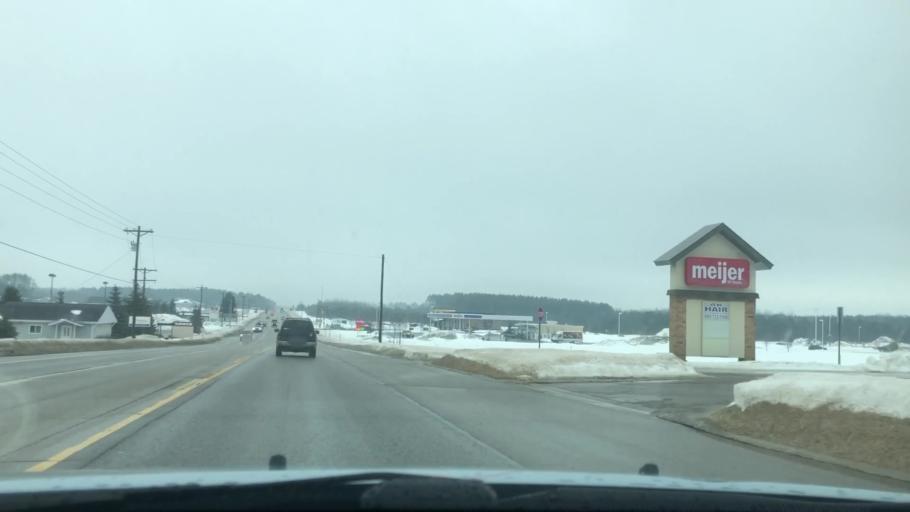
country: US
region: Michigan
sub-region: Otsego County
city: Gaylord
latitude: 45.0271
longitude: -84.7259
